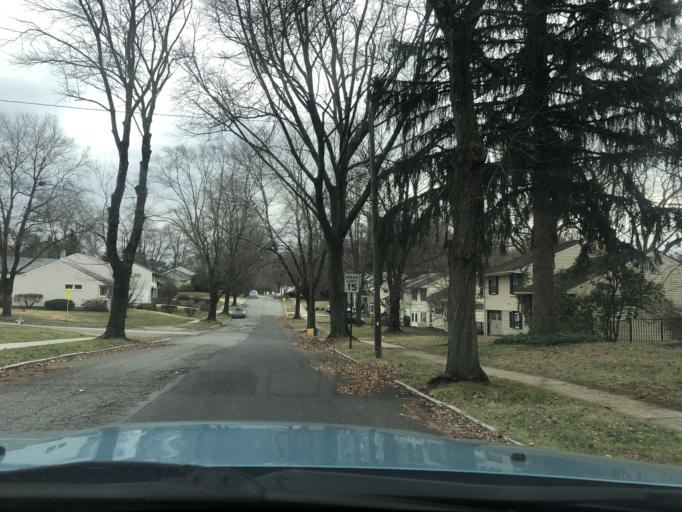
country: US
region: Pennsylvania
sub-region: Delaware County
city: Radnor
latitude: 40.0234
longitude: -75.3424
